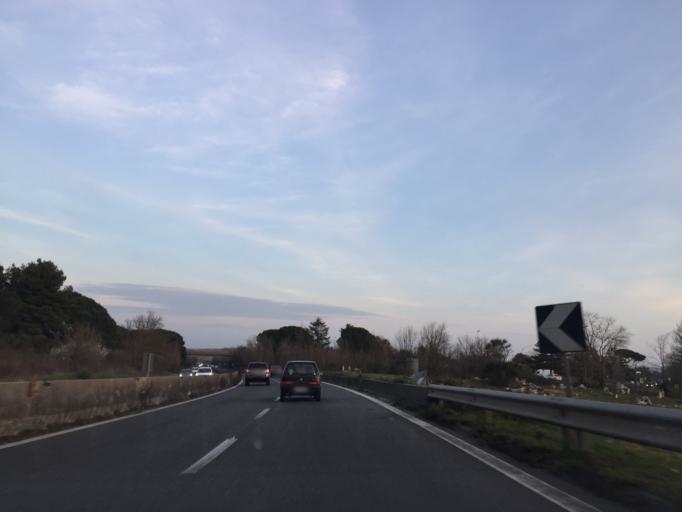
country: IT
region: Latium
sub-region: Citta metropolitana di Roma Capitale
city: Le Rughe
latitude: 42.0544
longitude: 12.3736
